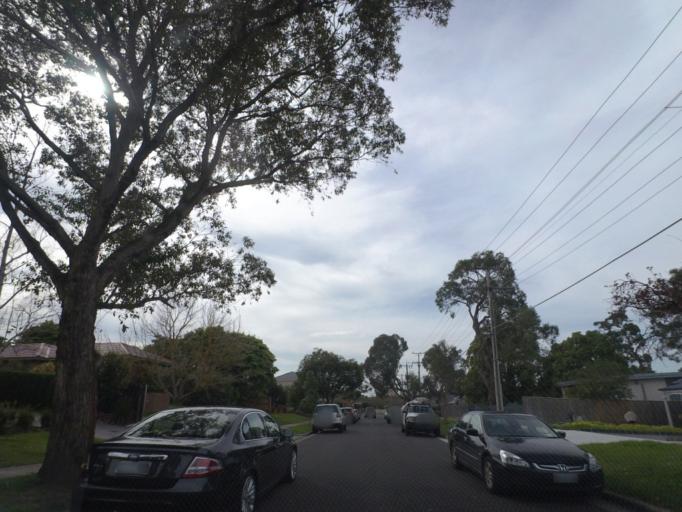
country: AU
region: Victoria
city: Mitcham
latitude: -37.8280
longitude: 145.2030
